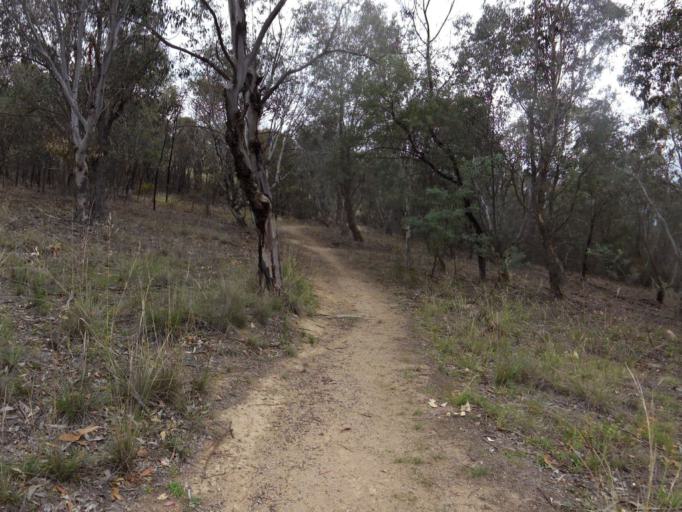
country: AU
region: Australian Capital Territory
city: Forrest
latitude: -35.3570
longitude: 149.0300
